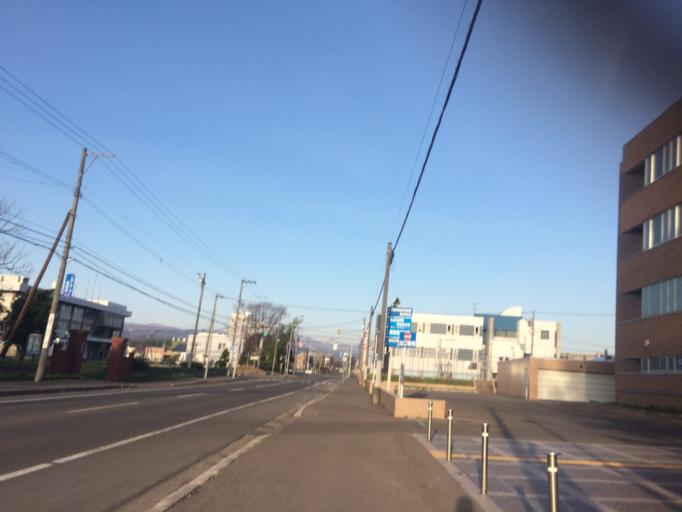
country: JP
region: Hokkaido
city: Niseko Town
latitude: 42.9011
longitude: 140.7571
